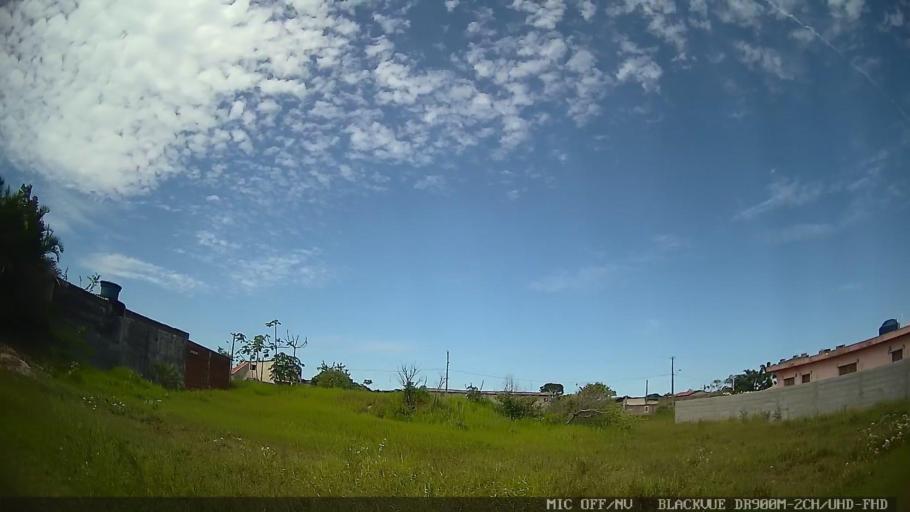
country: BR
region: Sao Paulo
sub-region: Iguape
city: Iguape
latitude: -24.7217
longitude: -47.5304
